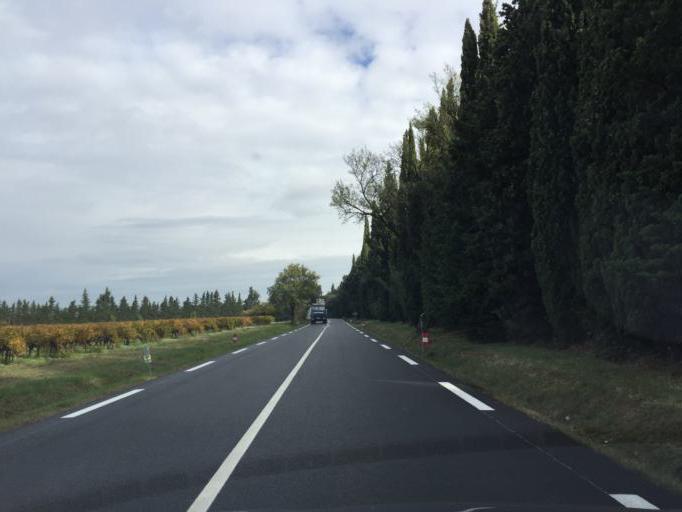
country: FR
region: Provence-Alpes-Cote d'Azur
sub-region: Departement du Vaucluse
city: Orange
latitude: 44.1714
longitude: 4.8125
